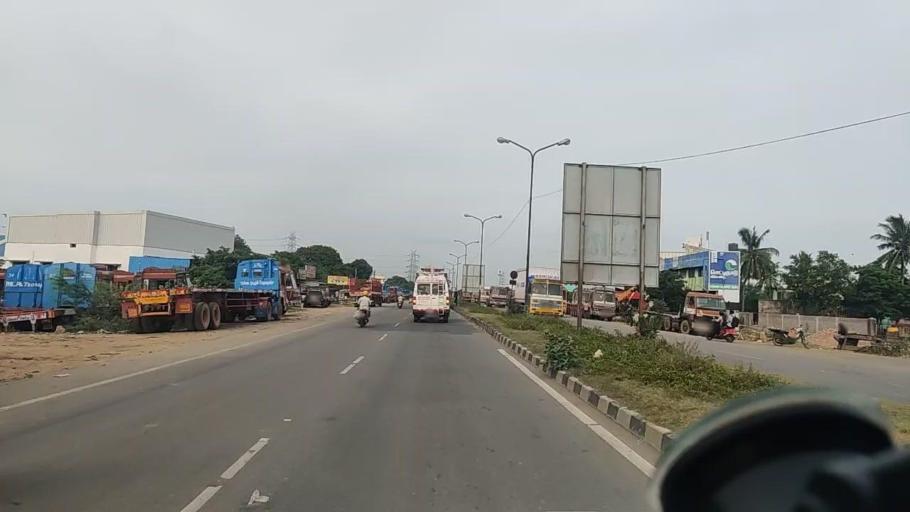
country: IN
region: Tamil Nadu
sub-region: Thiruvallur
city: Chinnasekkadu
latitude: 13.1776
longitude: 80.2476
